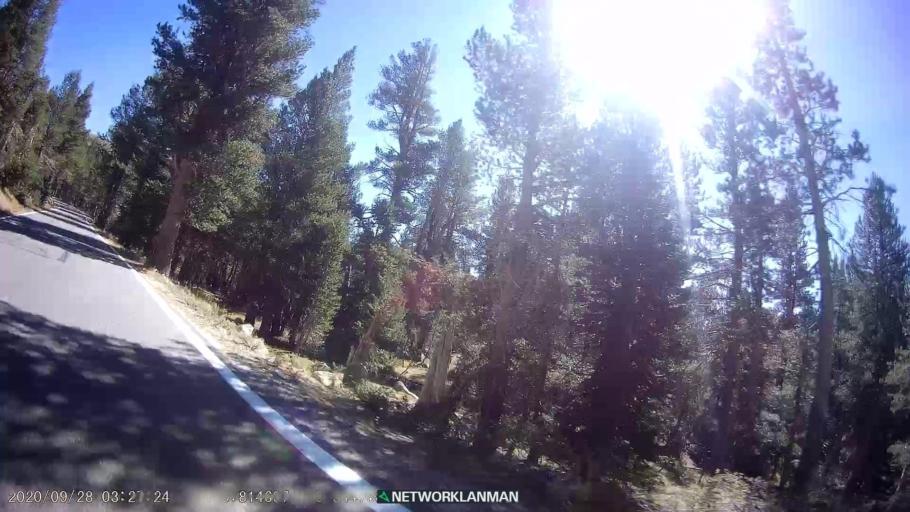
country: US
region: Nevada
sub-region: Douglas County
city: Gardnerville Ranchos
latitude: 38.5448
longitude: -119.8145
